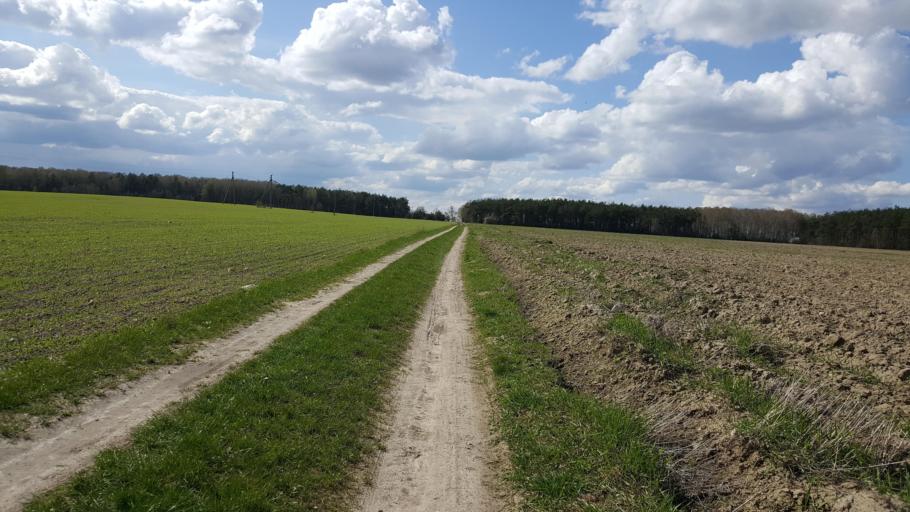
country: BY
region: Brest
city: Kamyanyets
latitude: 52.3901
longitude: 23.6472
